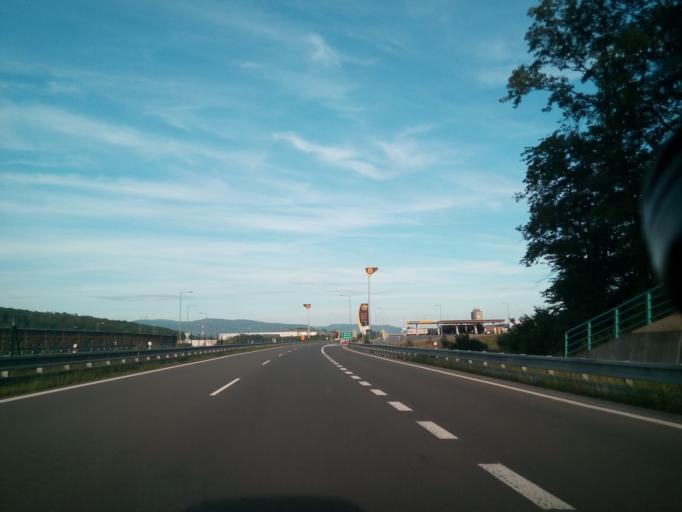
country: SK
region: Presovsky
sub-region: Okres Presov
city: Presov
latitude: 49.0020
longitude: 21.1816
